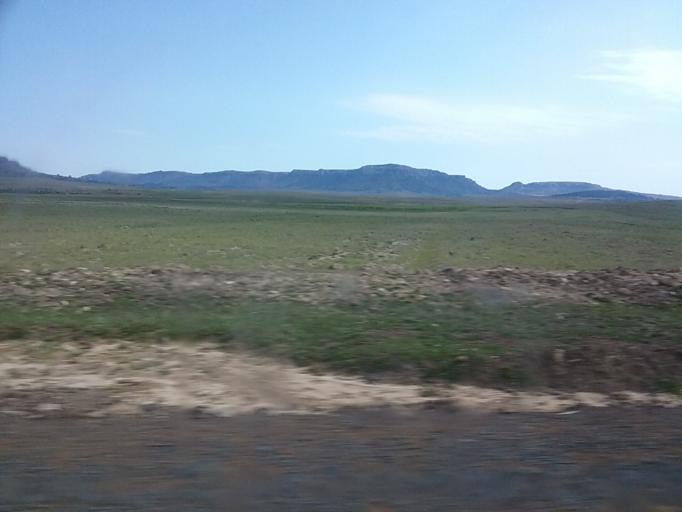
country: LS
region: Berea
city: Teyateyaneng
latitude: -29.0850
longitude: 27.8974
